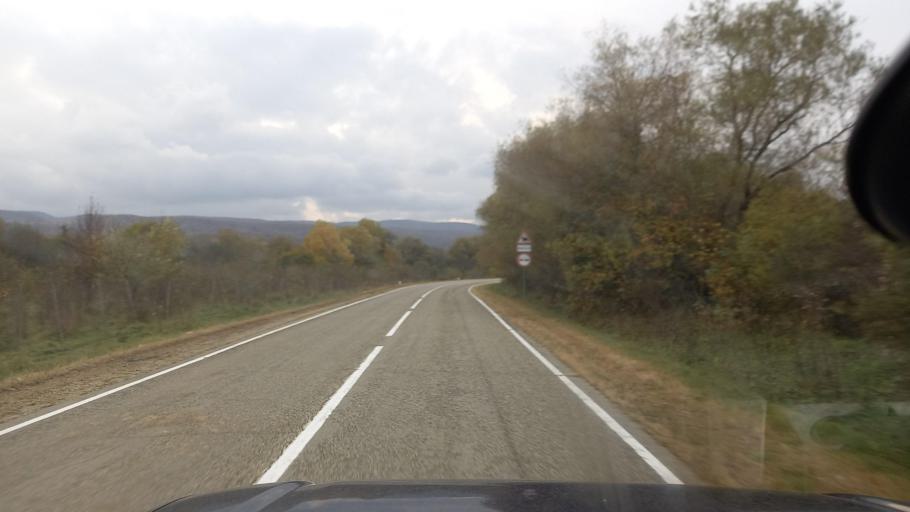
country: RU
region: Krasnodarskiy
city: Gubskaya
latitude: 44.2974
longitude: 40.5483
